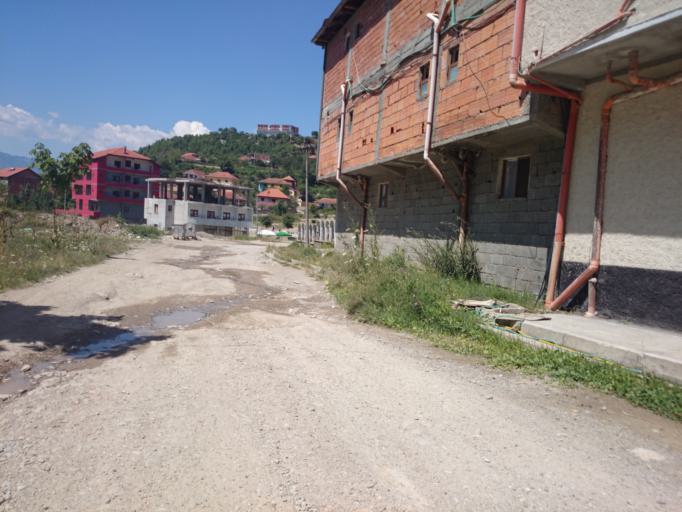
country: AL
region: Diber
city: Peshkopi
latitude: 41.6854
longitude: 20.4489
